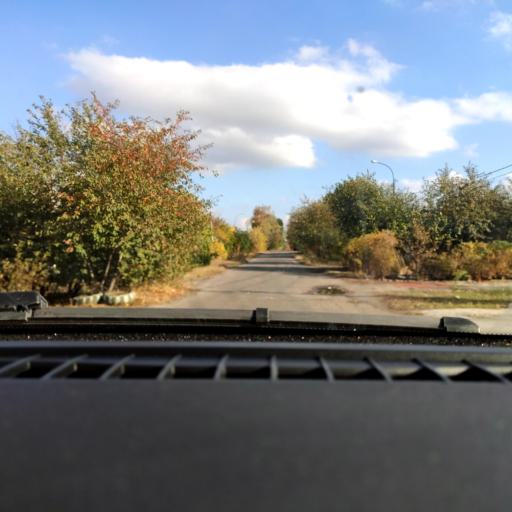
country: RU
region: Voronezj
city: Maslovka
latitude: 51.6159
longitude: 39.2655
